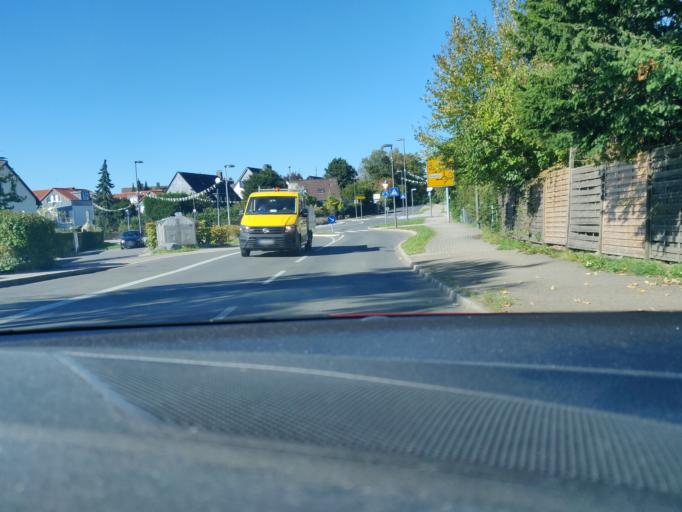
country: DE
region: North Rhine-Westphalia
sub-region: Regierungsbezirk Dusseldorf
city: Heiligenhaus
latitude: 51.3469
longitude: 6.9527
